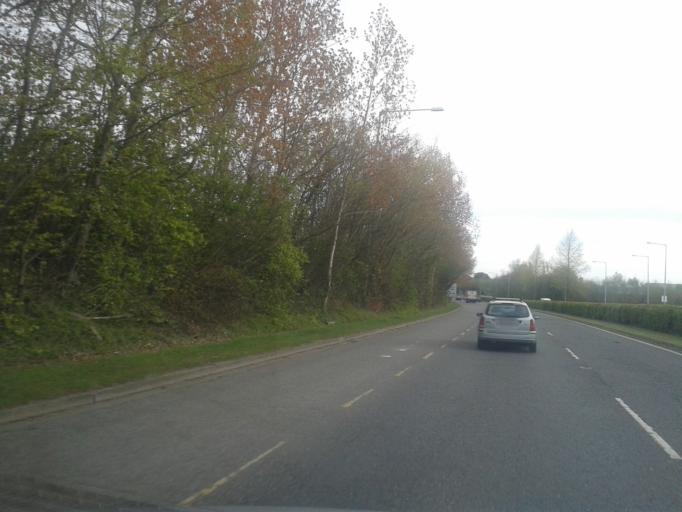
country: IE
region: Leinster
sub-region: Fingal County
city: Swords
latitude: 53.4571
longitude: -6.2128
